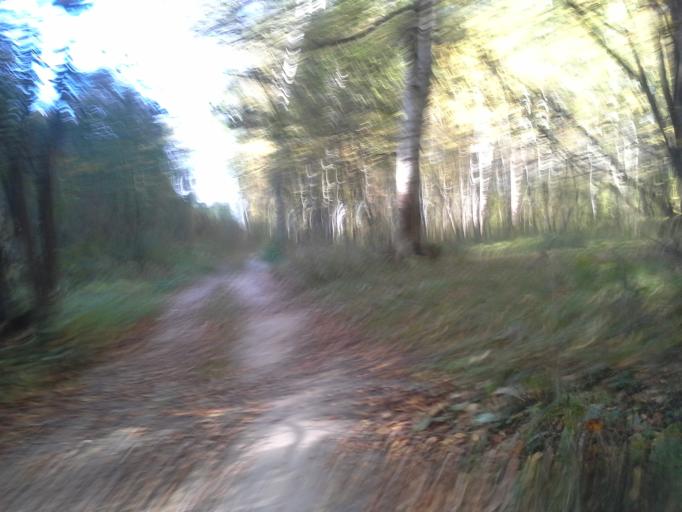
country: RU
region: Moskovskaya
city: Kommunarka
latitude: 55.5507
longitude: 37.4668
